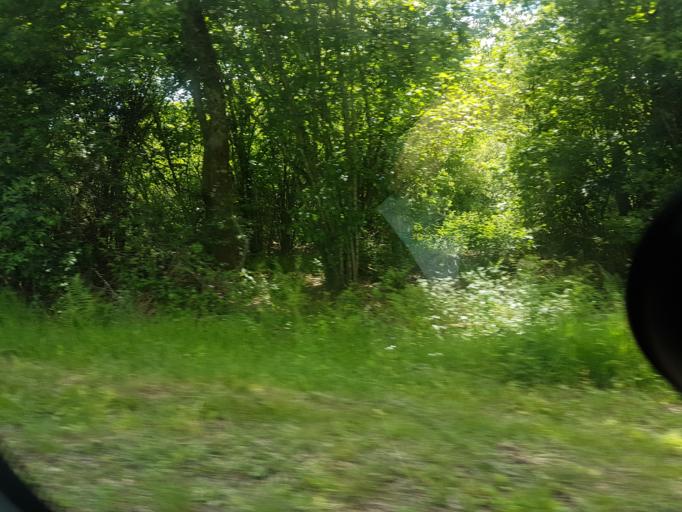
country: FR
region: Bourgogne
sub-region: Departement de la Cote-d'Or
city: Saulieu
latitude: 47.1768
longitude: 4.1154
